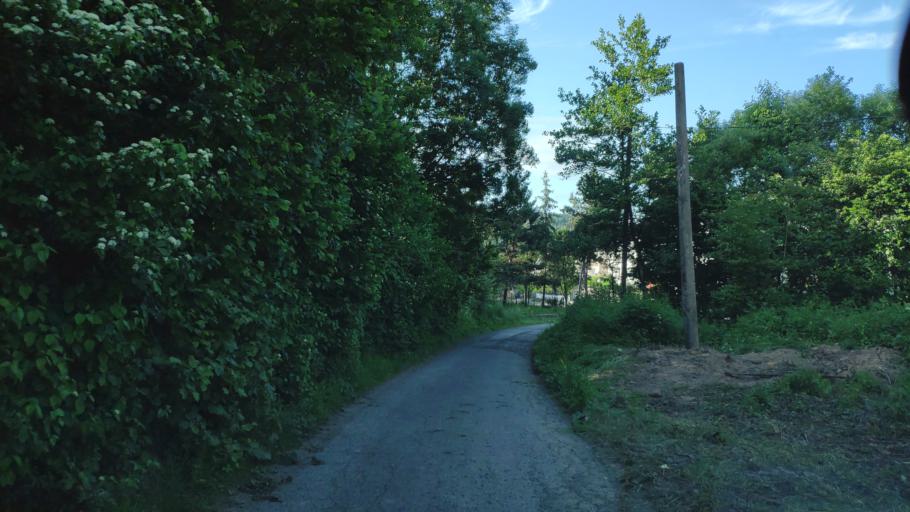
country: SK
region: Presovsky
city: Vranov nad Topl'ou
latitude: 48.8265
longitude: 21.5771
